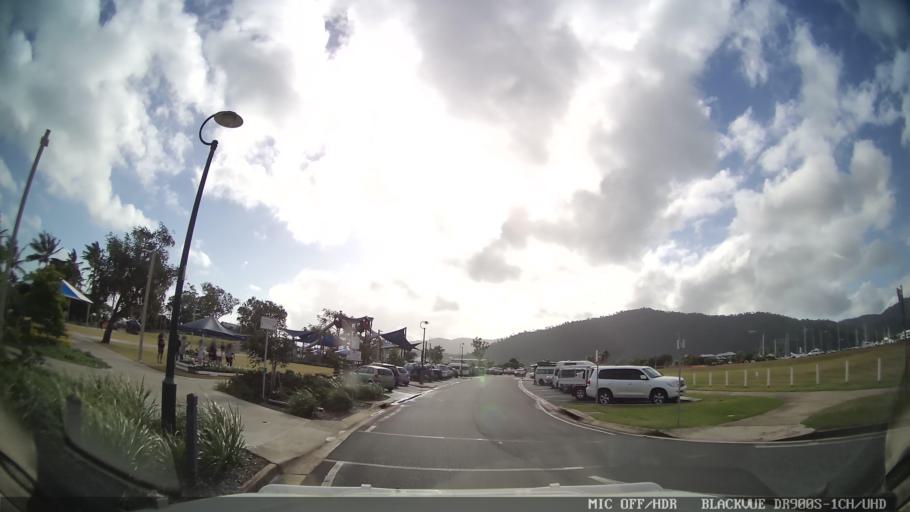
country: AU
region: Queensland
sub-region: Whitsunday
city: Proserpine
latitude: -20.2690
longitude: 148.7219
